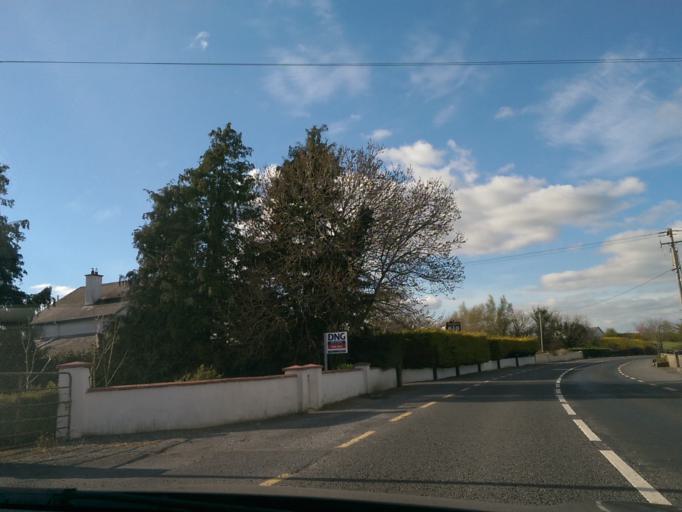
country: IE
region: Connaught
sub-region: County Galway
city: Portumna
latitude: 53.1057
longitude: -8.2357
